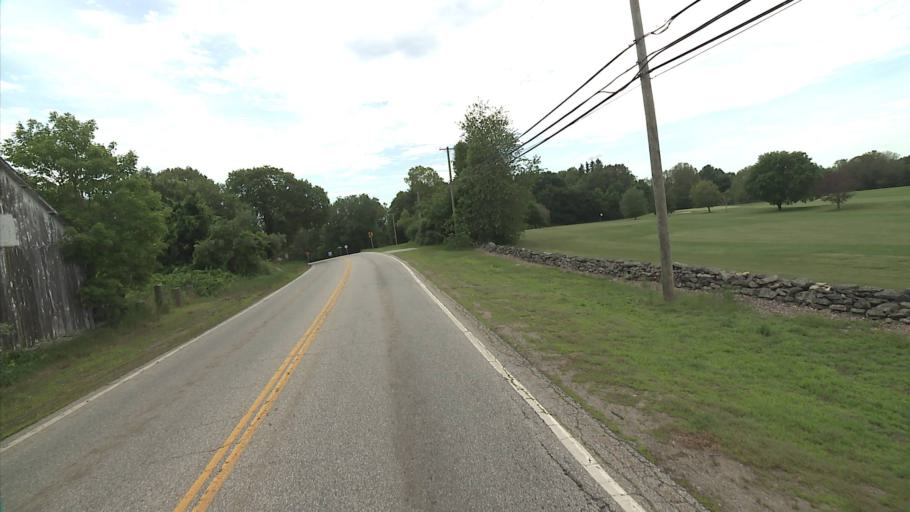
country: US
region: Connecticut
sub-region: New London County
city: Jewett City
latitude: 41.5773
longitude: -71.9772
